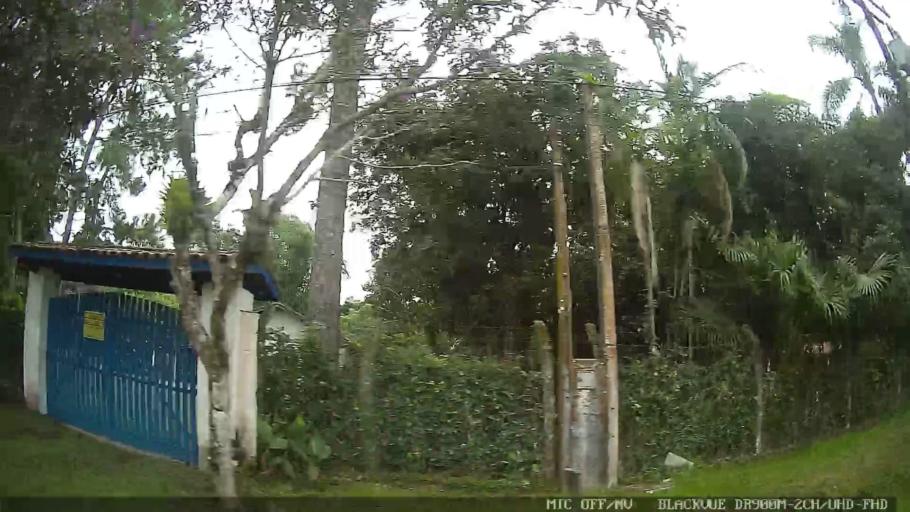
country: BR
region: Sao Paulo
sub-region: Iguape
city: Iguape
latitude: -24.6912
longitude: -47.5269
